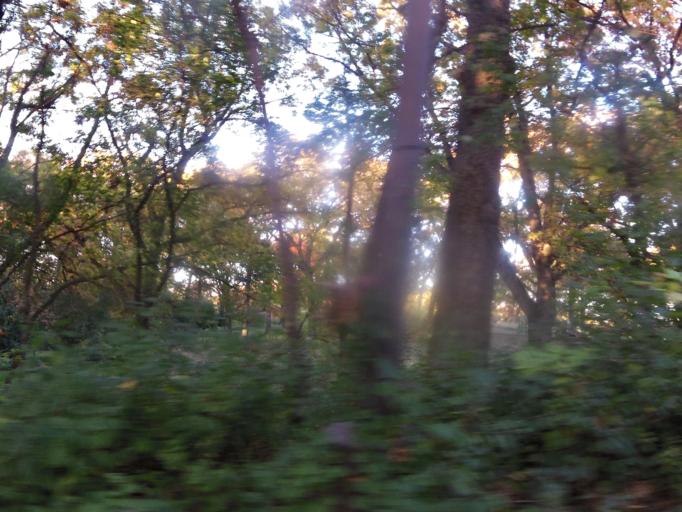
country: US
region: Minnesota
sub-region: Washington County
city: Lake Elmo
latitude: 44.9771
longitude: -92.8755
